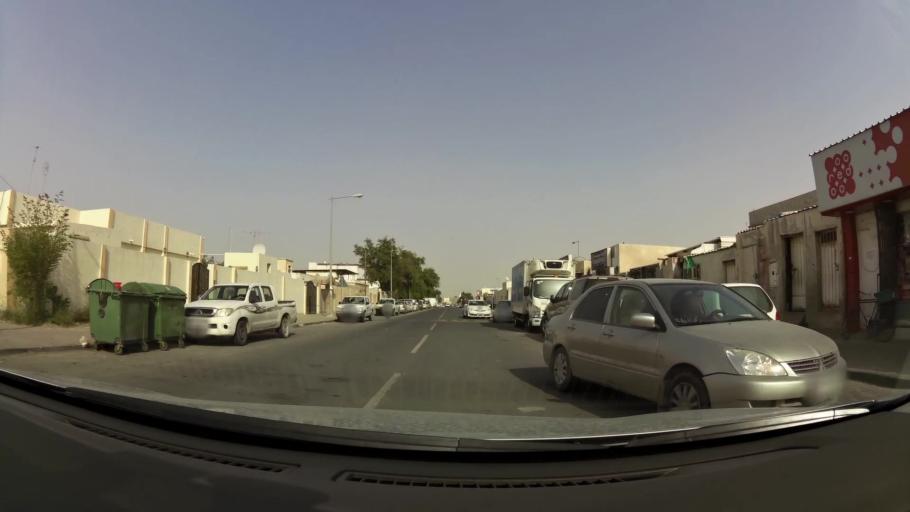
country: QA
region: Baladiyat ar Rayyan
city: Ar Rayyan
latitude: 25.2390
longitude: 51.4346
